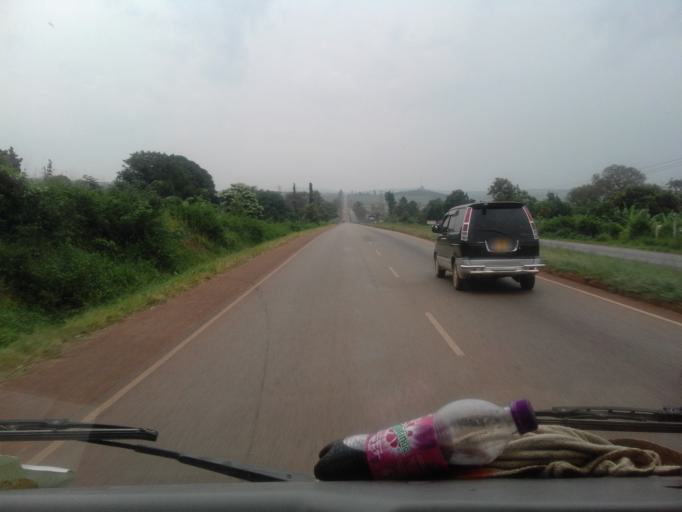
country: UG
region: Eastern Region
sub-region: Jinja District
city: Bugembe
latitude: 0.4798
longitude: 33.2728
